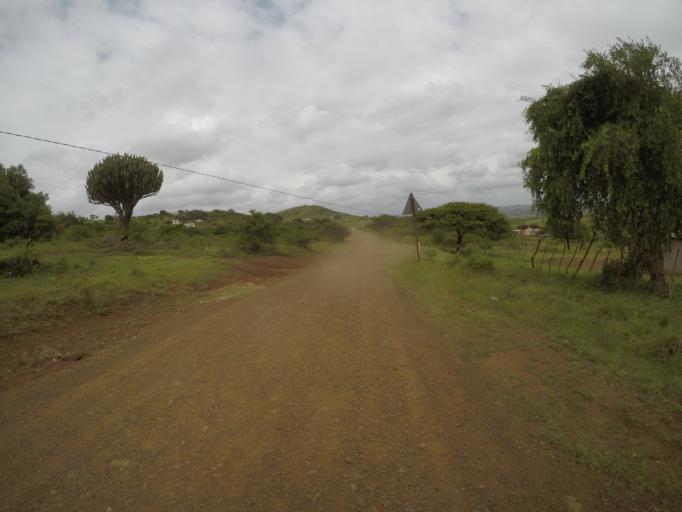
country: ZA
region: KwaZulu-Natal
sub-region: uThungulu District Municipality
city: Empangeni
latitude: -28.6135
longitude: 31.8980
